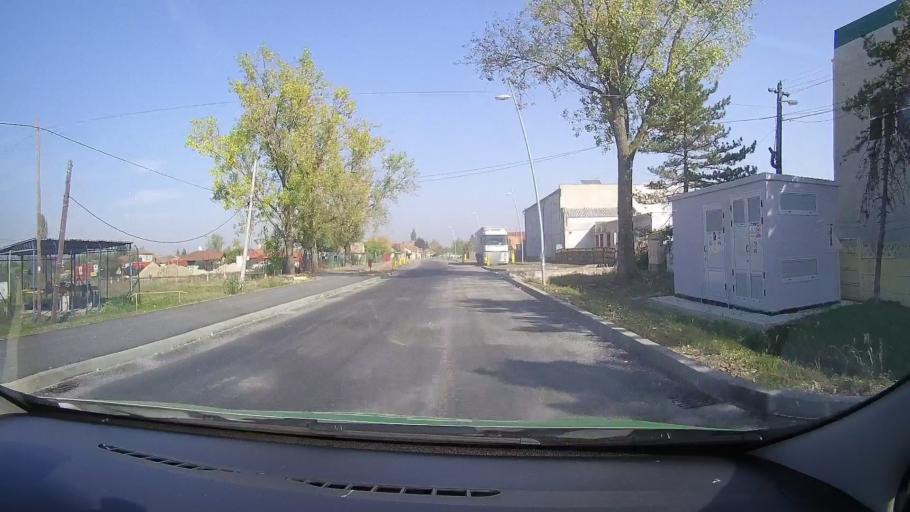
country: RO
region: Bihor
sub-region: Municipiul Salonta
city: Salonta
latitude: 46.7928
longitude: 21.6645
